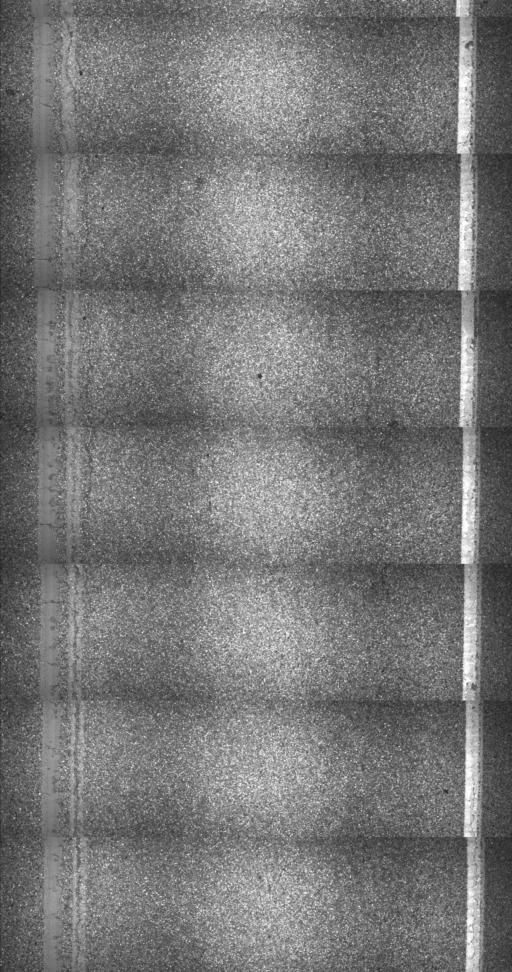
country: US
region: Vermont
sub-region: Bennington County
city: Manchester Center
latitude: 43.1974
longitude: -73.0530
